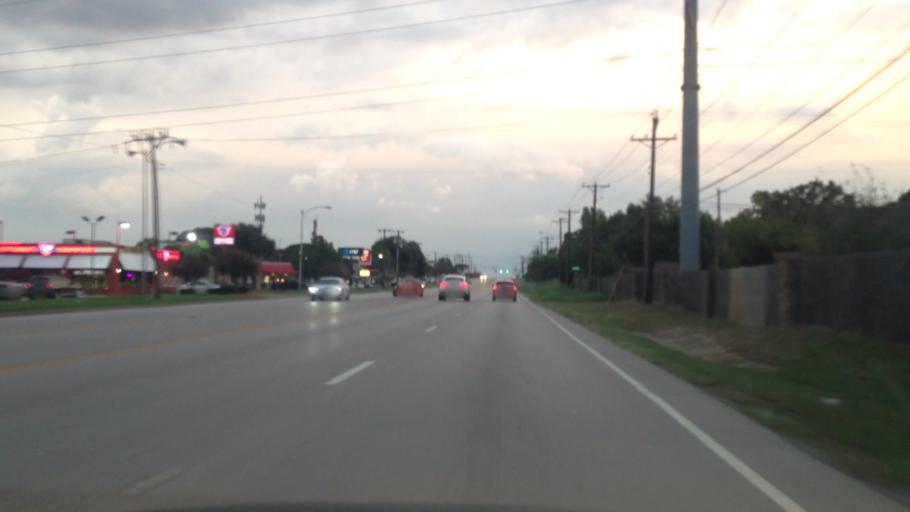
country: US
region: Texas
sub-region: Tarrant County
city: Colleyville
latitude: 32.8637
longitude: -97.1764
